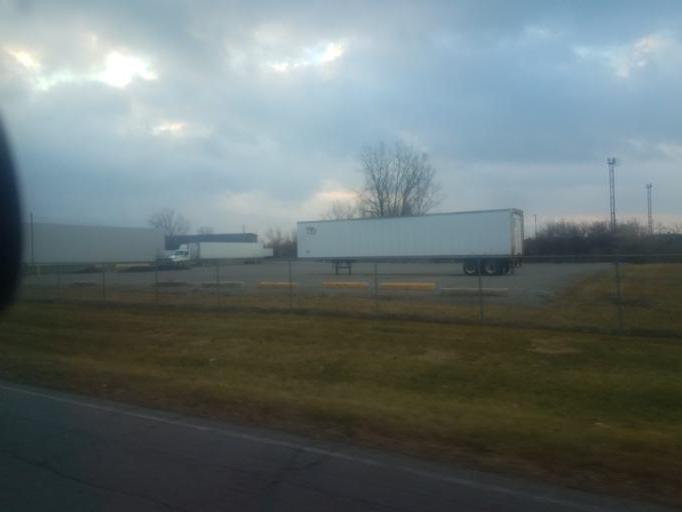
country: US
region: Ohio
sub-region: Marion County
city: Marion
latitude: 40.5930
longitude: -83.1602
